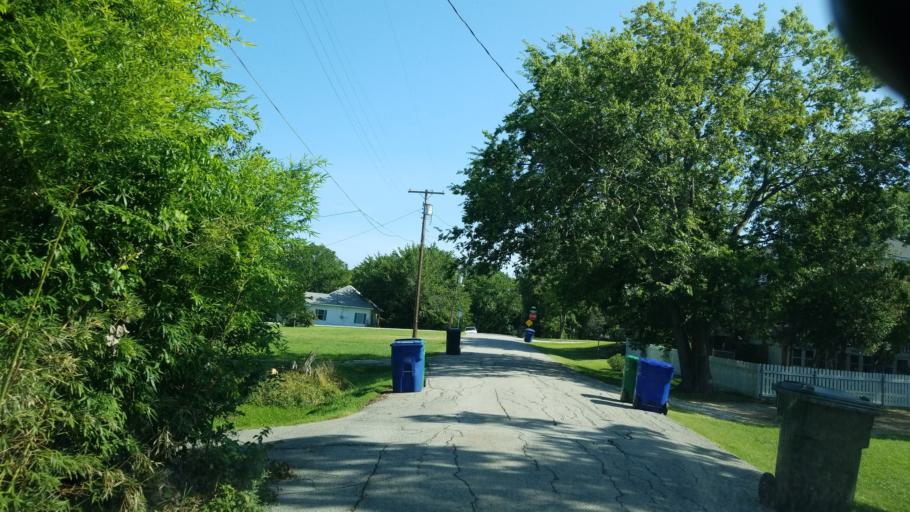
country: US
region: Texas
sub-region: Dallas County
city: Carrollton
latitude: 32.9567
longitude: -96.9015
